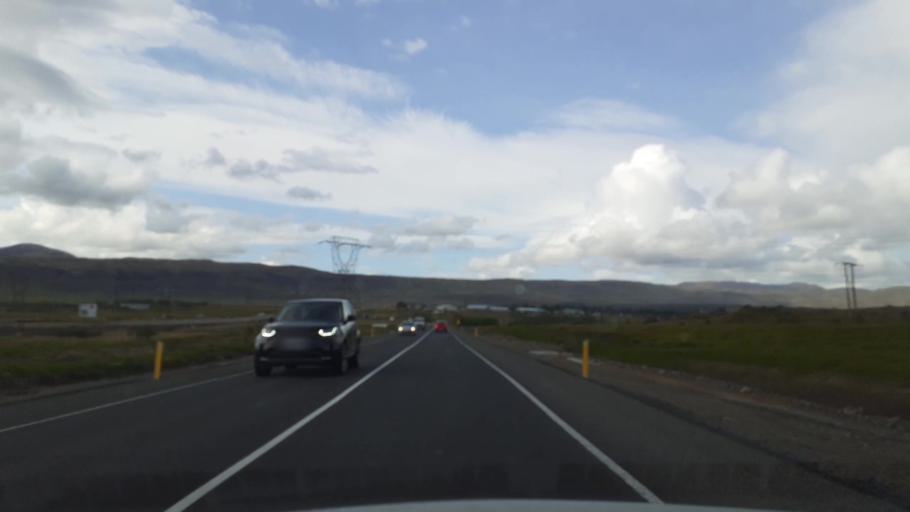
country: IS
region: South
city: Hveragerdi
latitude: 63.9874
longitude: -21.1617
